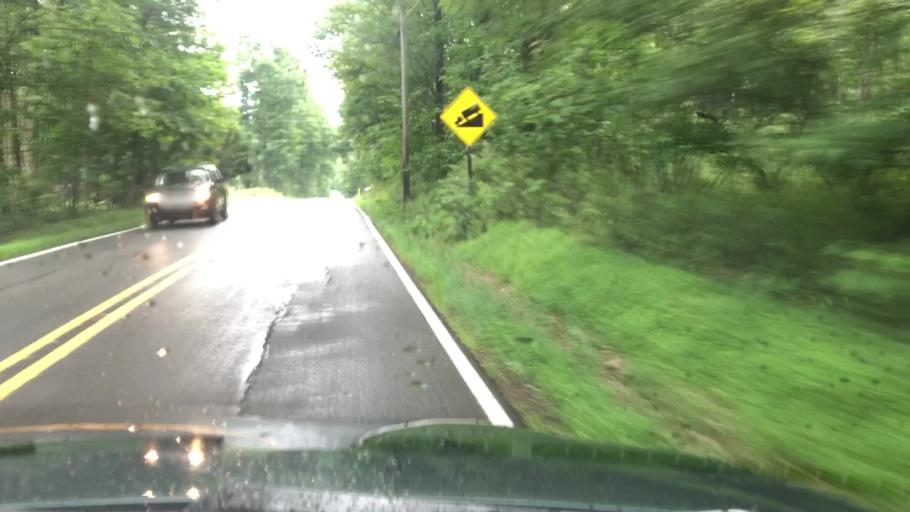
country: US
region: Pennsylvania
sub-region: Monroe County
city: Mountainhome
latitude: 41.2718
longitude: -75.2441
